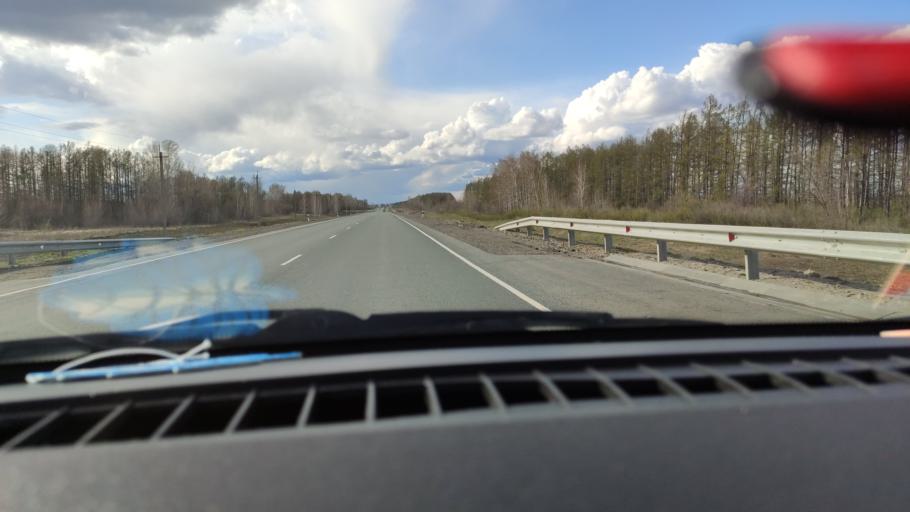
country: RU
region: Saratov
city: Shikhany
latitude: 52.1564
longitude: 47.1773
